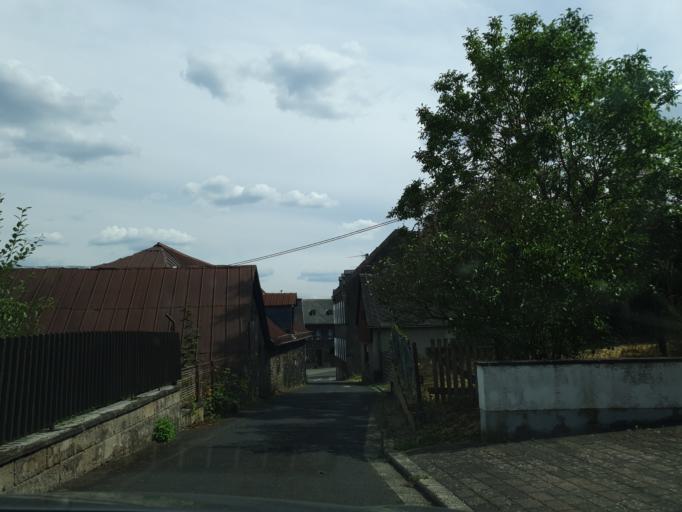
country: DE
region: Rheinland-Pfalz
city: Boos
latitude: 50.3139
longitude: 7.0164
